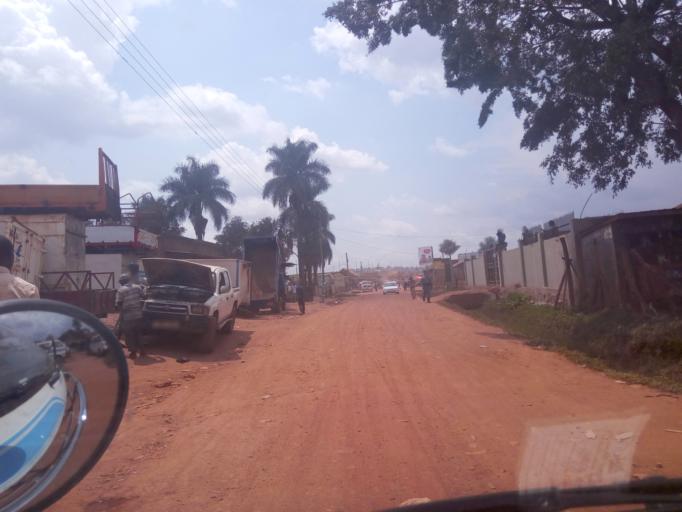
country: UG
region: Central Region
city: Kampala Central Division
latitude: 0.3481
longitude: 32.5598
